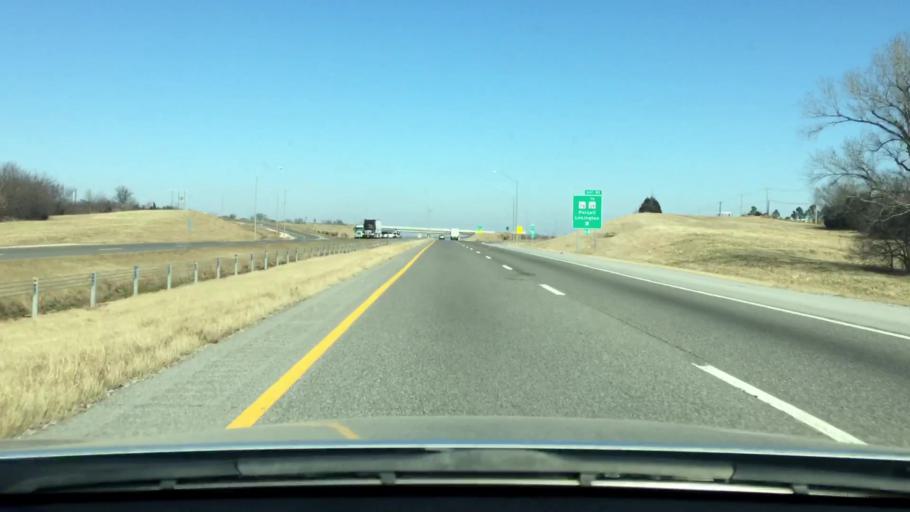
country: US
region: Oklahoma
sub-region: McClain County
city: Purcell
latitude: 34.9778
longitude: -97.3718
